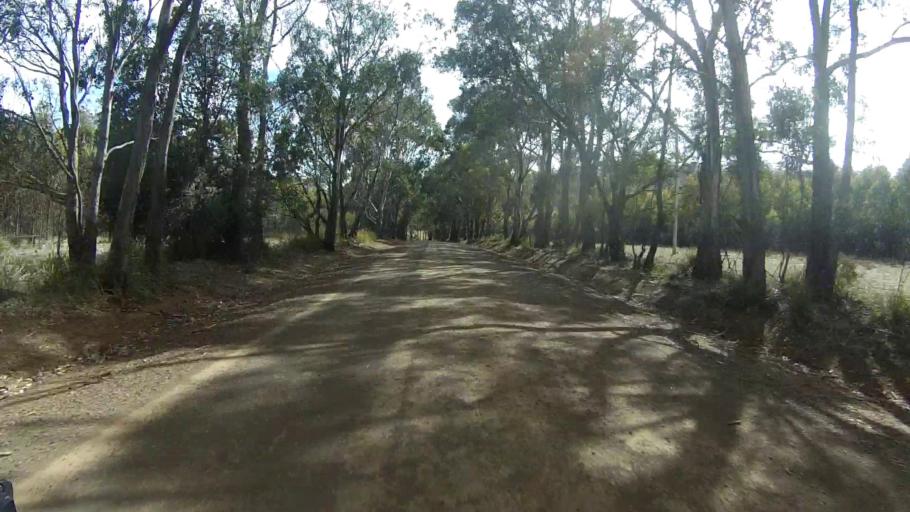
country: AU
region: Tasmania
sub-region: Sorell
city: Sorell
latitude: -42.6610
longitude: 147.8943
